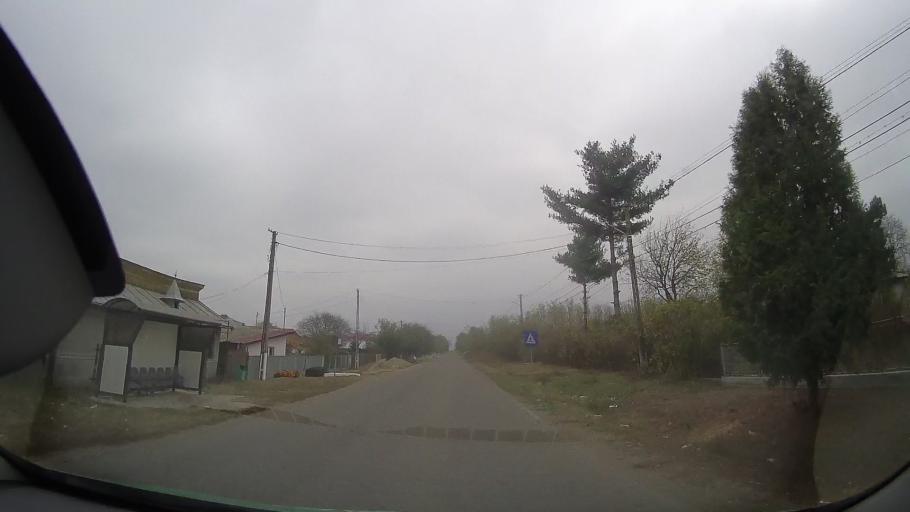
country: RO
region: Buzau
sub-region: Comuna Glodeanu-Silistea
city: Glodeanu-Silistea
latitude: 44.8202
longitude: 26.8355
